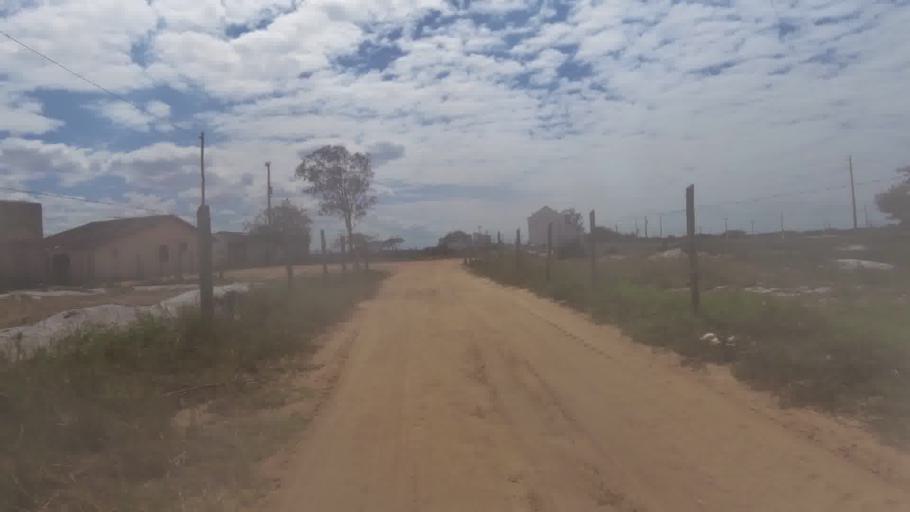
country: BR
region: Espirito Santo
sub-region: Marataizes
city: Marataizes
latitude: -21.2365
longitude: -40.9928
